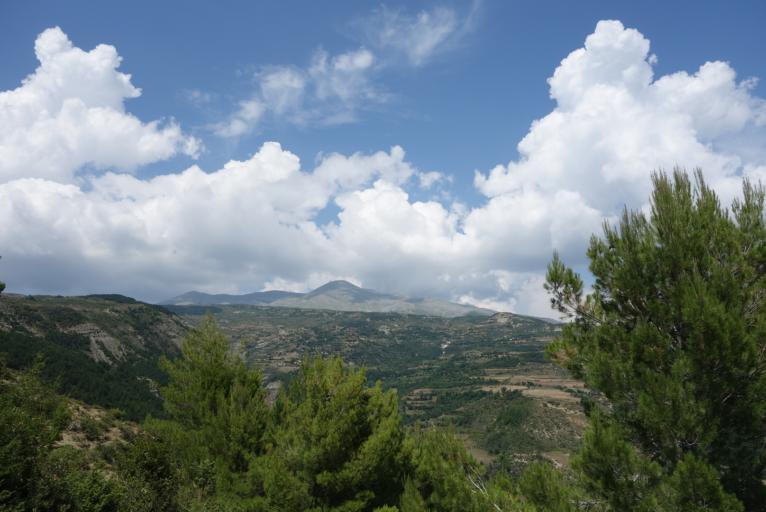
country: AL
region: Berat
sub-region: Rrethi i Skraparit
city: Corovode
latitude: 40.5186
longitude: 20.2158
